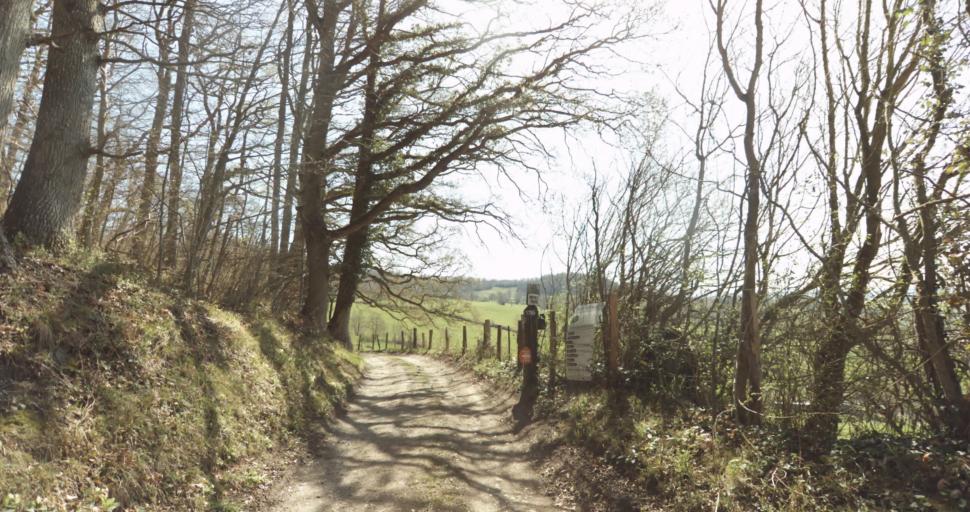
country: FR
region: Lower Normandy
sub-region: Departement du Calvados
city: Saint-Pierre-sur-Dives
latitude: 49.0033
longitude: 0.0423
